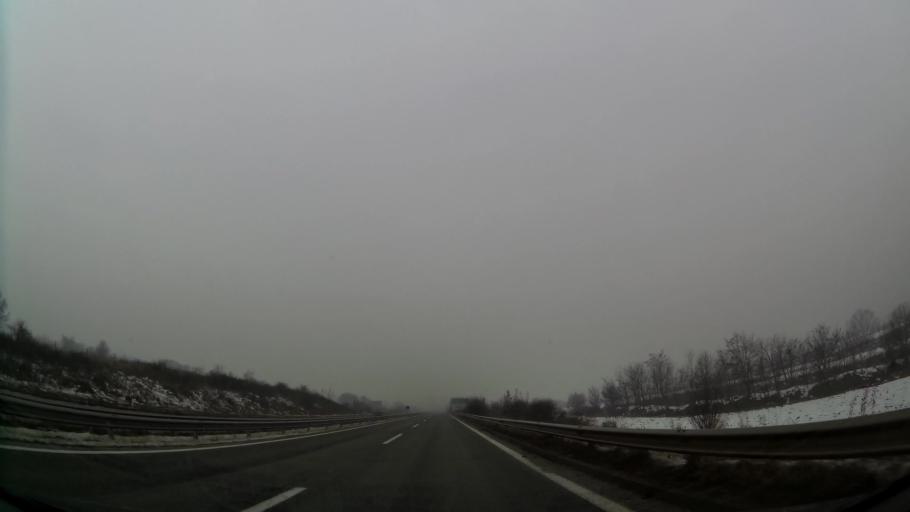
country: MK
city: Miladinovci
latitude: 41.9660
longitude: 21.6401
